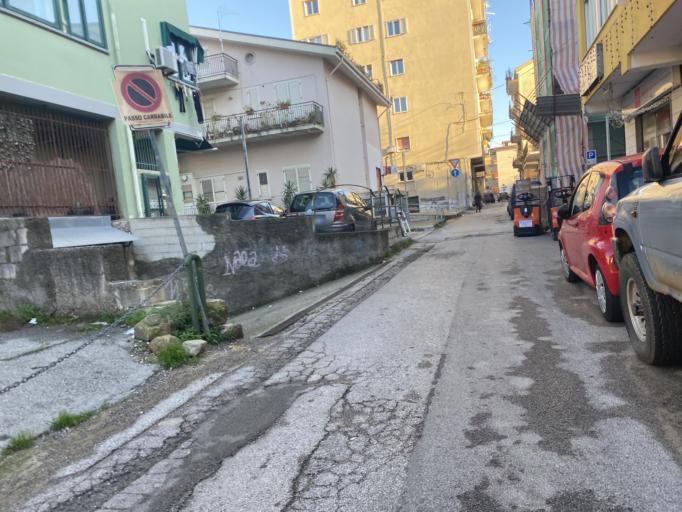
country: IT
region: Campania
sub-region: Provincia di Salerno
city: Agropoli
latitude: 40.3503
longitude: 14.9883
